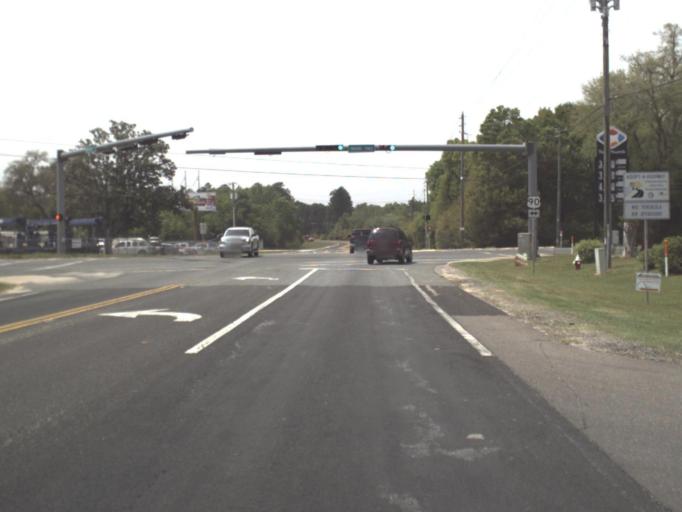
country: US
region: Florida
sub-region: Escambia County
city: Bellview
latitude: 30.4870
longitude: -87.3156
